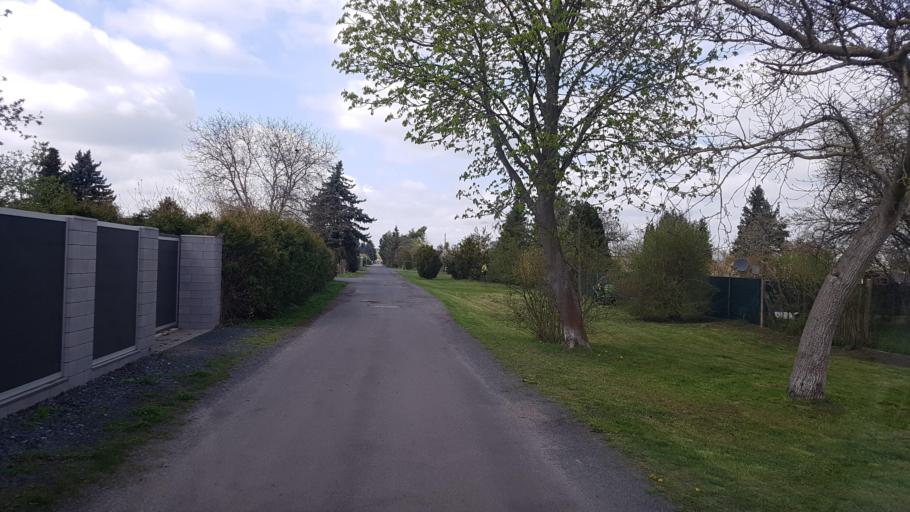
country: DE
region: Brandenburg
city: Luckenwalde
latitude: 52.1016
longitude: 13.1684
